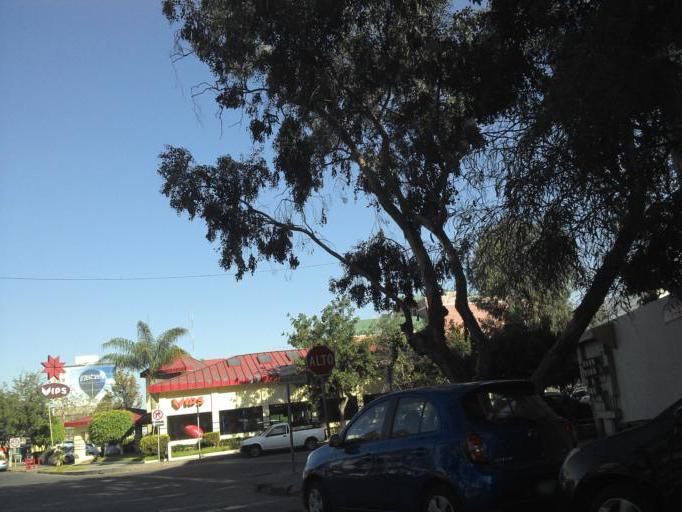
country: MX
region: Baja California
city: Tijuana
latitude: 32.5179
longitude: -117.0092
